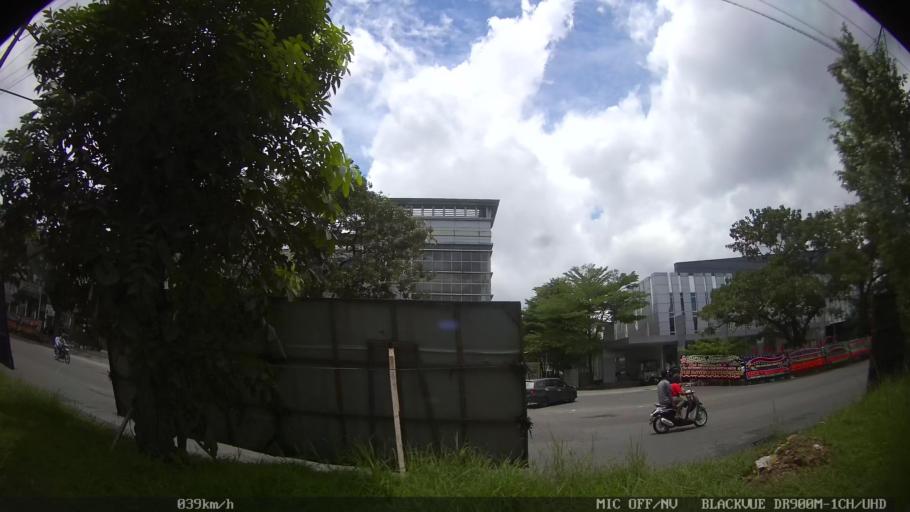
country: ID
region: North Sumatra
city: Medan
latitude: 3.6105
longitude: 98.7122
